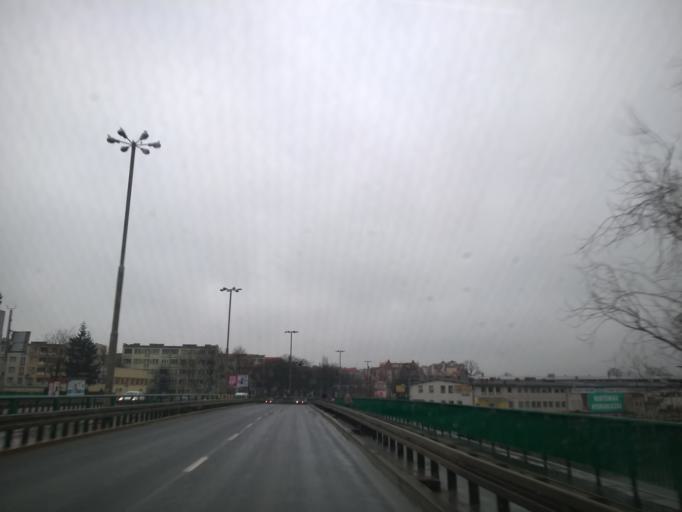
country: PL
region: Lower Silesian Voivodeship
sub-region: Powiat wroclawski
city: Wroclaw
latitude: 51.1176
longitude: 17.0180
